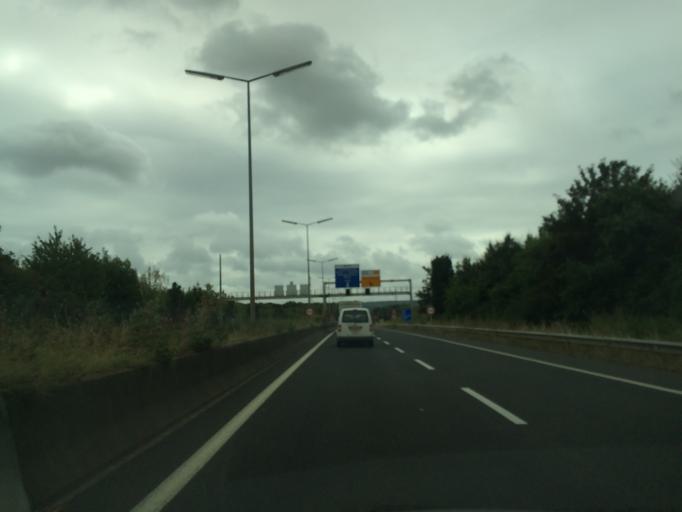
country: LU
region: Luxembourg
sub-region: Canton d'Esch-sur-Alzette
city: Mondercange
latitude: 49.5206
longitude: 5.9710
